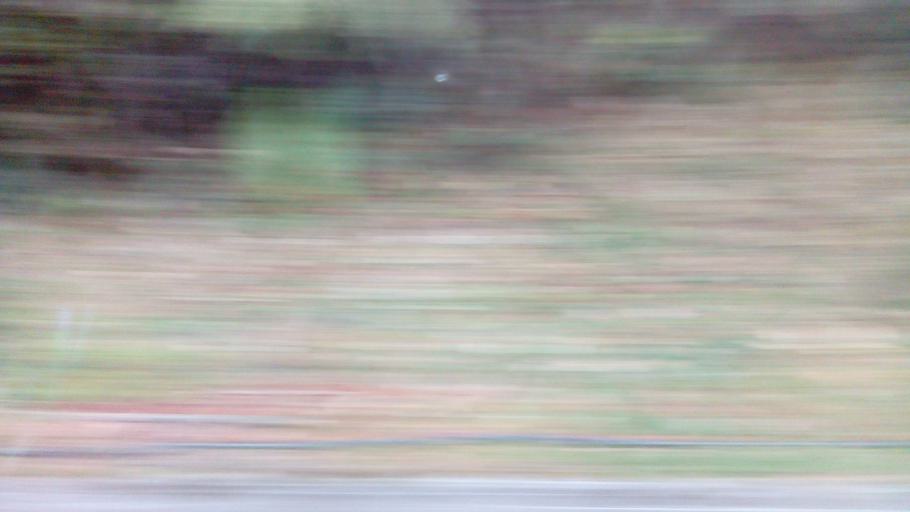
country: TW
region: Taiwan
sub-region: Hualien
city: Hualian
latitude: 24.3707
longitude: 121.3393
